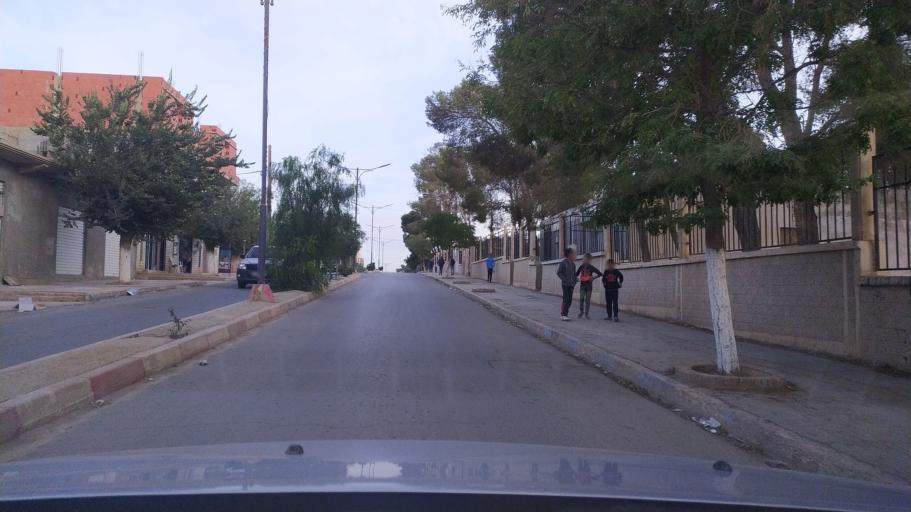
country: DZ
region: Tiaret
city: Frenda
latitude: 34.8974
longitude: 1.2391
